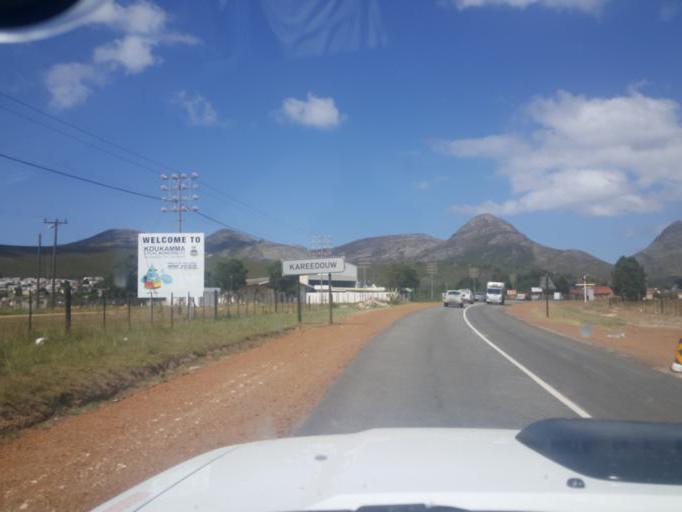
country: ZA
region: Eastern Cape
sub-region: Cacadu District Municipality
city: Kareedouw
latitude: -33.9518
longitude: 24.3000
